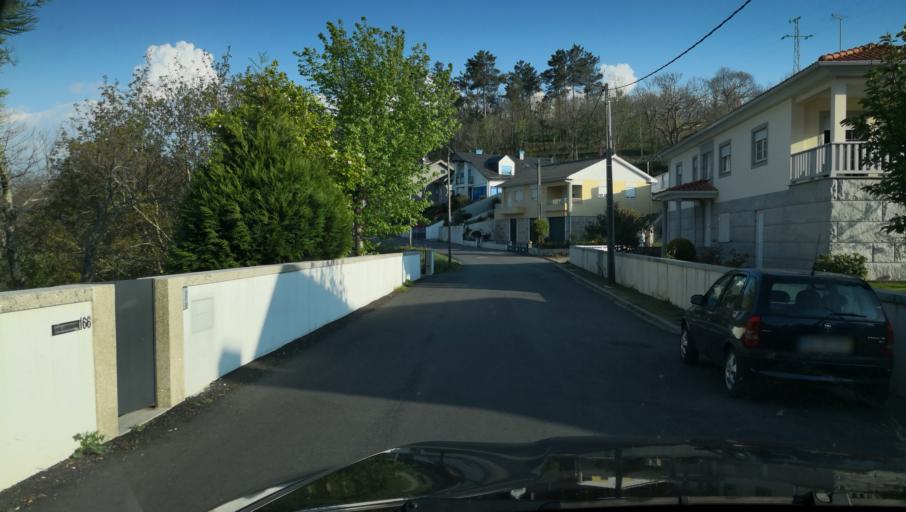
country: PT
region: Vila Real
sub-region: Santa Marta de Penaguiao
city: Santa Marta de Penaguiao
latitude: 41.2783
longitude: -7.8157
